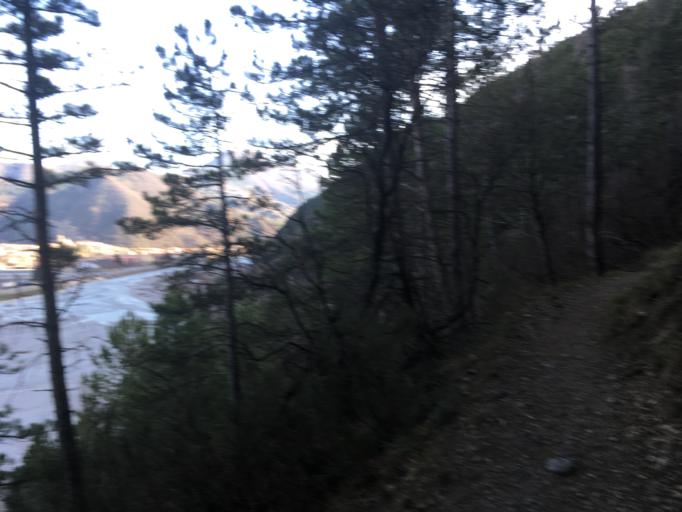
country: FR
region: Provence-Alpes-Cote d'Azur
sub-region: Departement des Alpes-de-Haute-Provence
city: Digne-les-Bains
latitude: 44.1058
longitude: 6.2264
